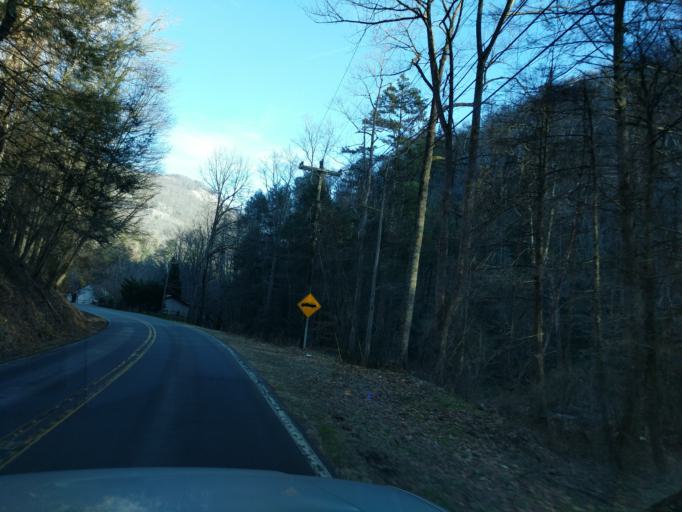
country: US
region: North Carolina
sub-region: Henderson County
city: Edneyville
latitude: 35.4521
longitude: -82.2941
